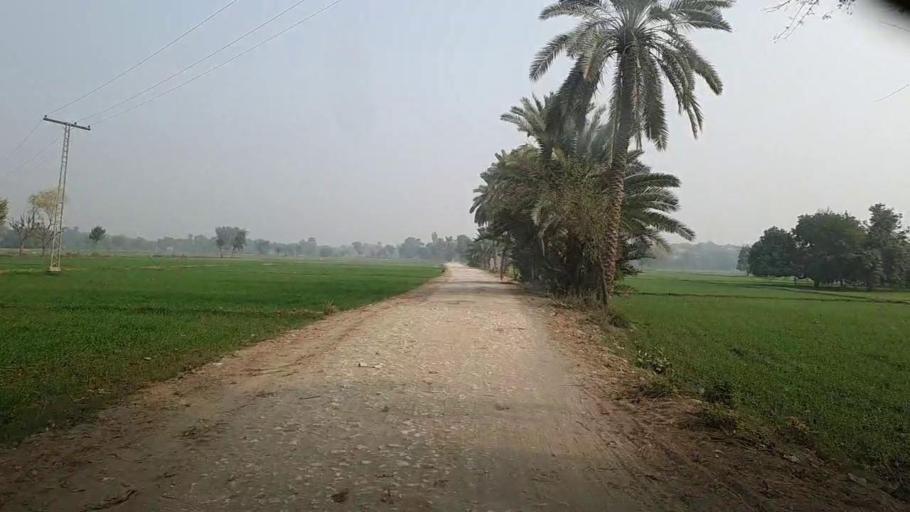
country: PK
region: Sindh
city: Bozdar
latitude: 27.1344
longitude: 68.6541
